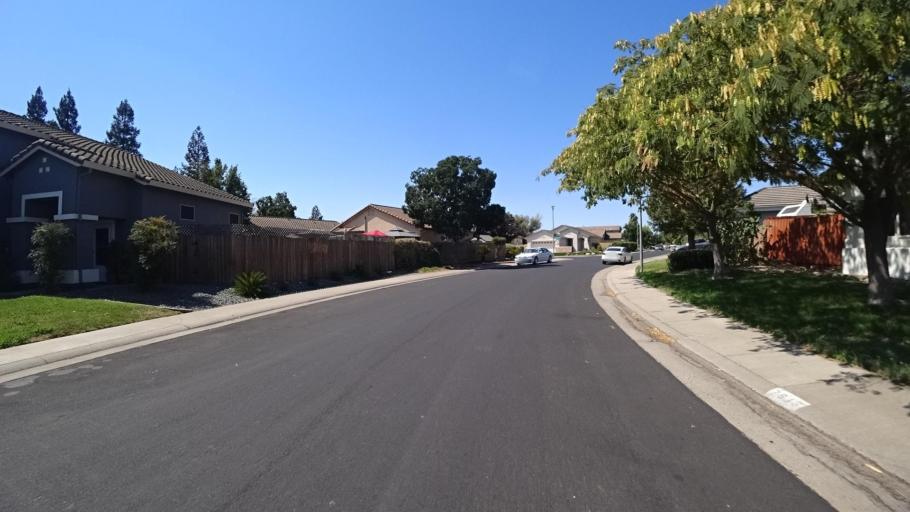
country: US
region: California
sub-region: Sacramento County
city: Laguna
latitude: 38.4102
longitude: -121.4116
